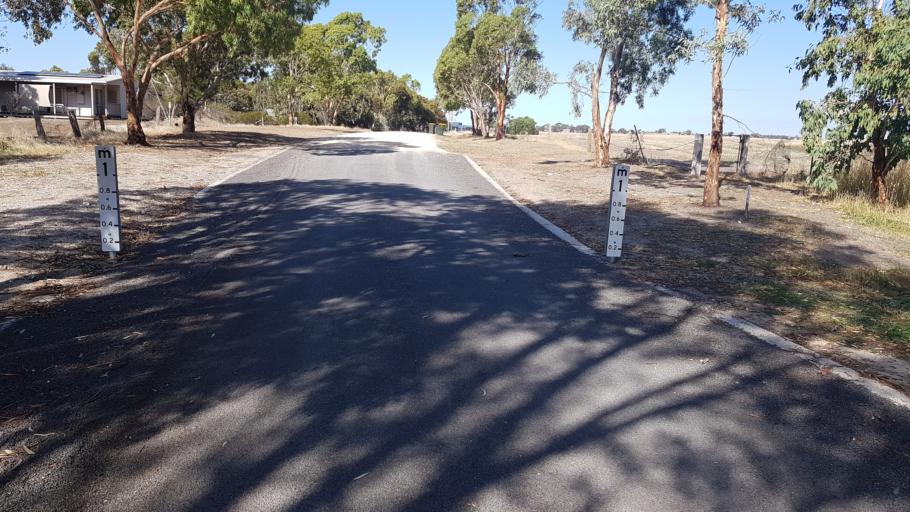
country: AU
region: Victoria
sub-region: Horsham
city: Horsham
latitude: -36.7434
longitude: 141.9433
